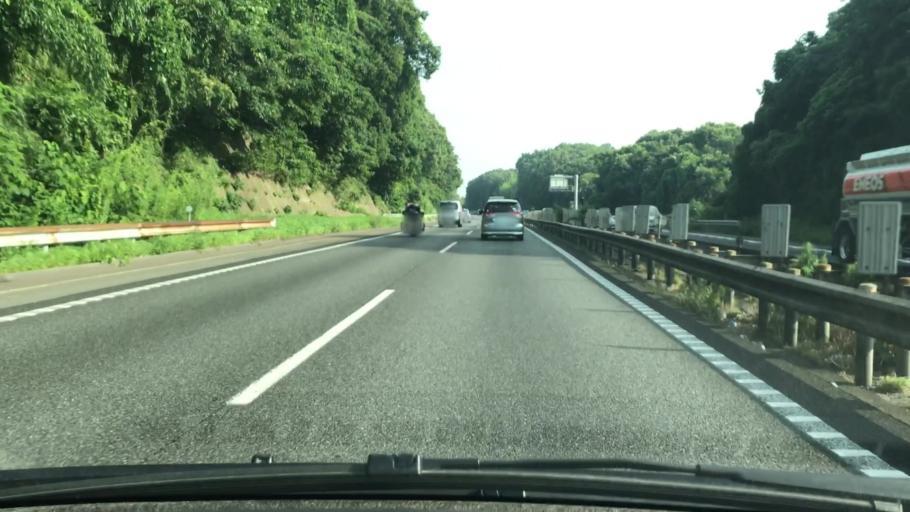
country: JP
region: Hyogo
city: Akashi
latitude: 34.6931
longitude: 134.9693
